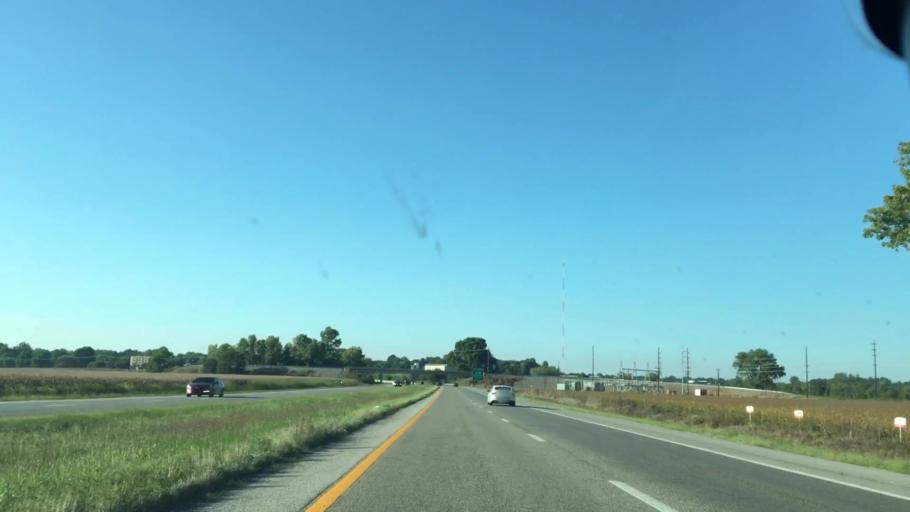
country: US
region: Kentucky
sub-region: Henderson County
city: Henderson
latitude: 37.8458
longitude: -87.5663
